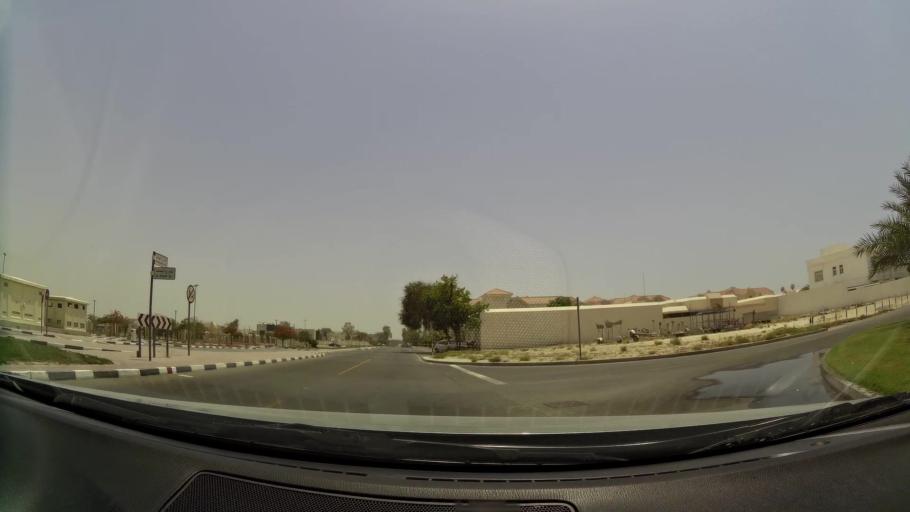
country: AE
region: Dubai
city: Dubai
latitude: 25.1663
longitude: 55.2170
